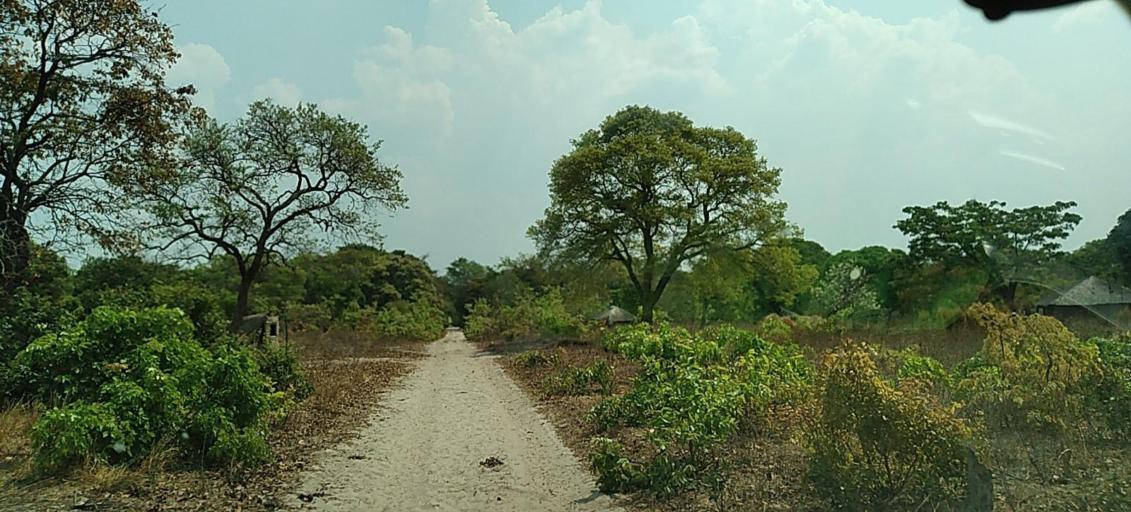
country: ZM
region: North-Western
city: Kabompo
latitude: -13.3863
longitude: 23.7667
